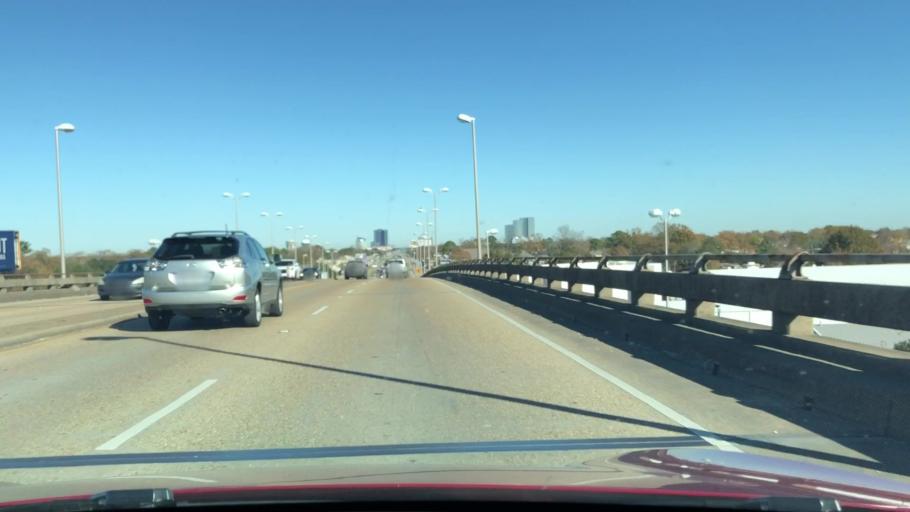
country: US
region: Louisiana
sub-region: Jefferson Parish
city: Metairie Terrace
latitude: 29.9750
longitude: -90.1563
